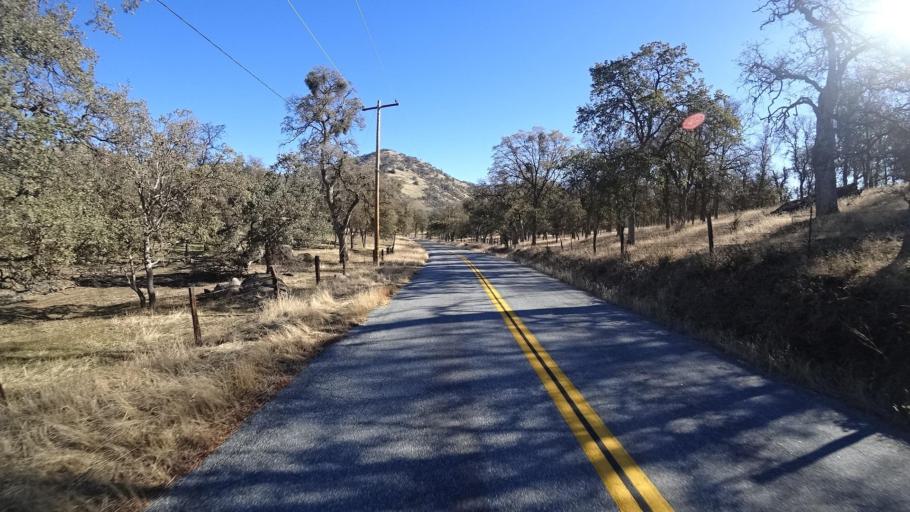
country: US
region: California
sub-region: Kern County
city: Alta Sierra
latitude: 35.7950
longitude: -118.7210
